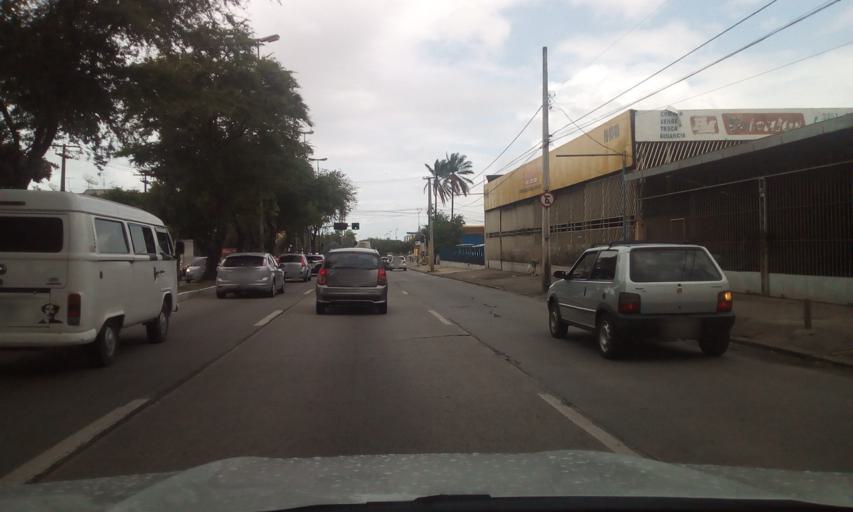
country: BR
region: Pernambuco
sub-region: Recife
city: Recife
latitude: -8.0951
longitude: -34.9289
